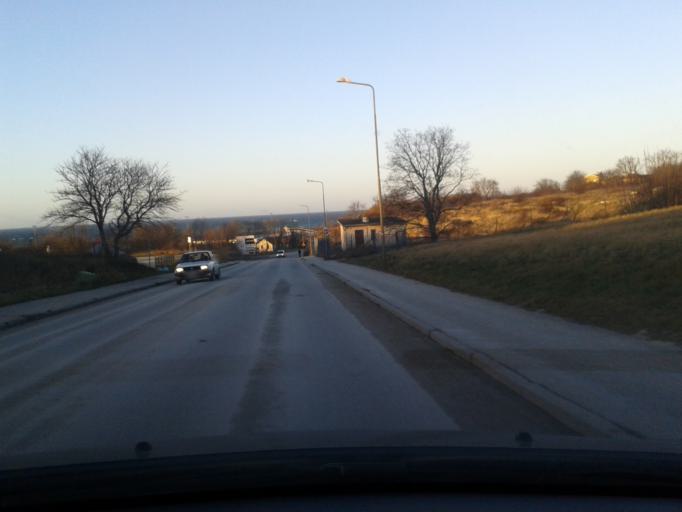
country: SE
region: Gotland
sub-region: Gotland
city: Visby
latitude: 57.6278
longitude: 18.2810
